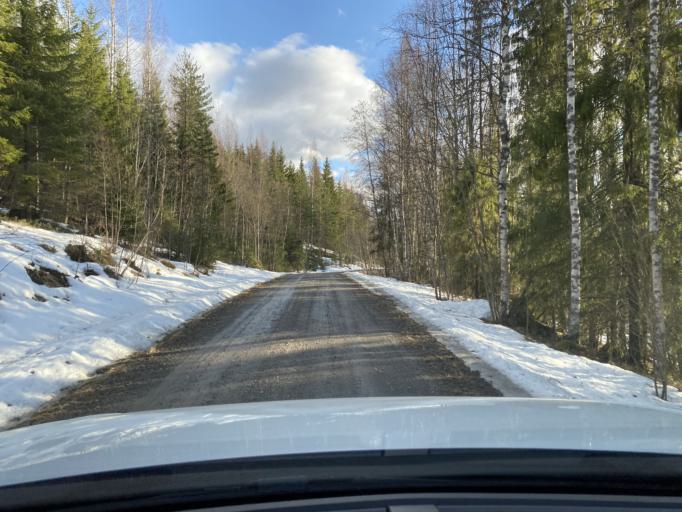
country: FI
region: Pirkanmaa
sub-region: Lounais-Pirkanmaa
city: Mouhijaervi
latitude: 61.4550
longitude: 22.9601
